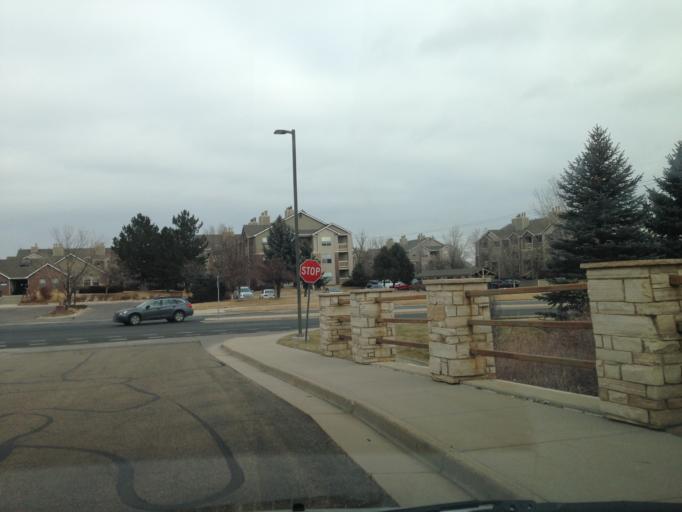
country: US
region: Colorado
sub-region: Boulder County
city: Superior
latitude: 39.9579
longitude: -105.1575
